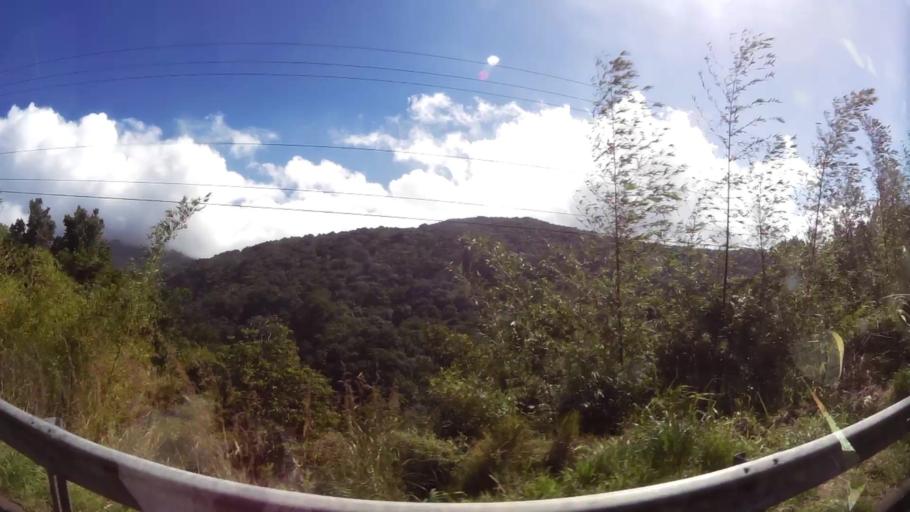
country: DM
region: Saint Paul
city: Pont Casse
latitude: 15.3523
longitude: -61.3595
